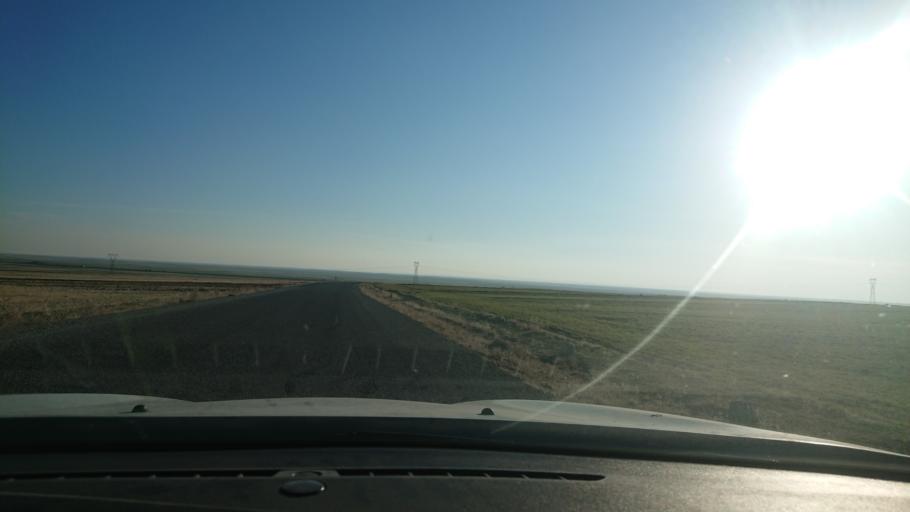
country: TR
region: Aksaray
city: Acipinar
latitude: 38.6764
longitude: 33.7312
